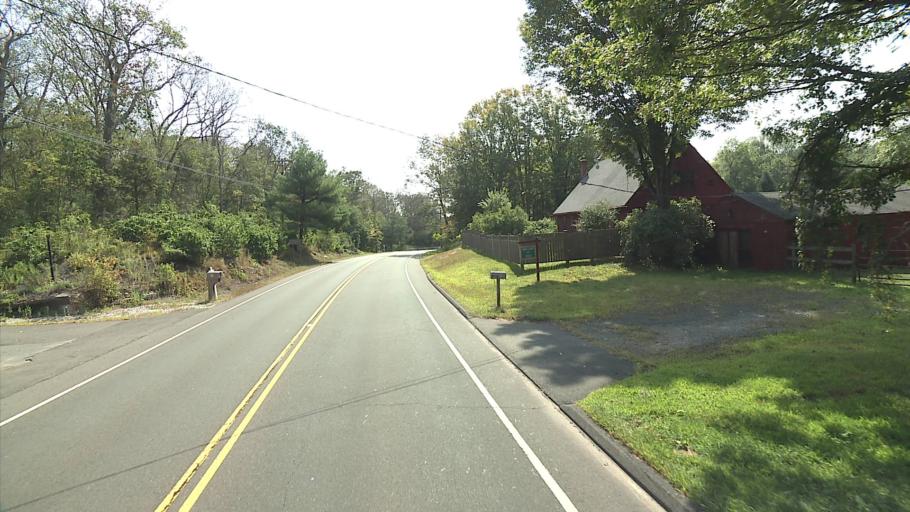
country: US
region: Connecticut
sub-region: Middlesex County
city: Durham
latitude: 41.4379
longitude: -72.6526
